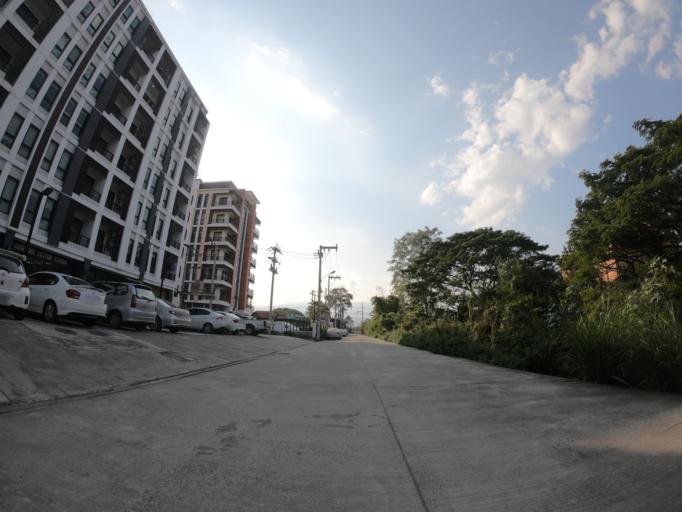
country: TH
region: Chiang Mai
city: Chiang Mai
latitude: 18.8200
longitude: 99.0130
